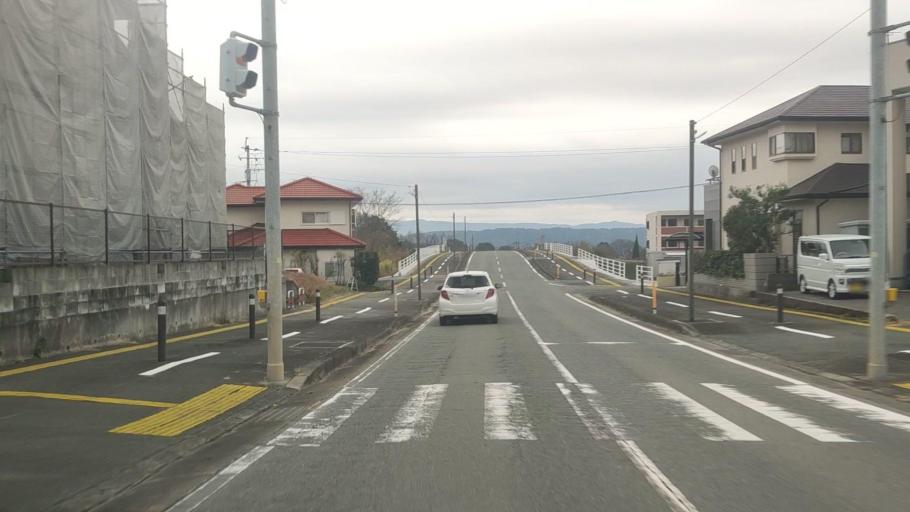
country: JP
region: Kumamoto
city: Ozu
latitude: 32.8771
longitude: 130.8939
